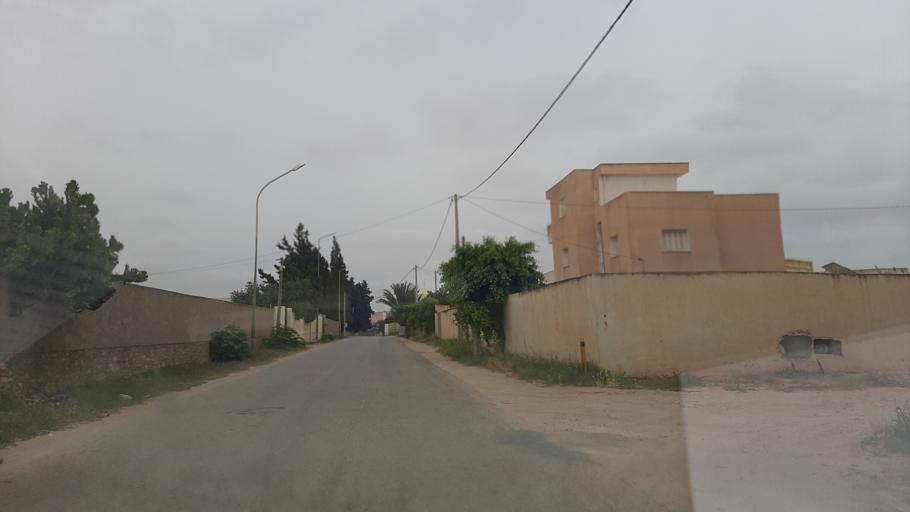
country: TN
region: Safaqis
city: Al Qarmadah
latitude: 34.7901
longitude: 10.7614
